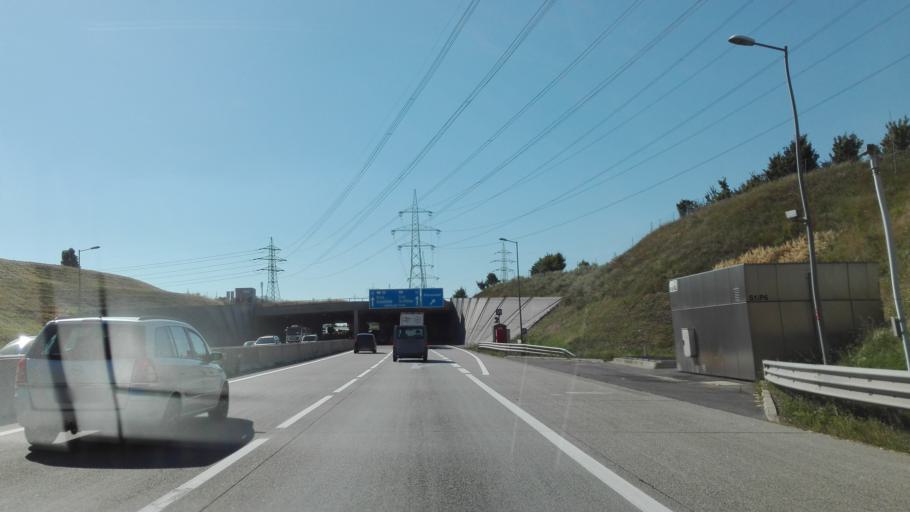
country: AT
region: Lower Austria
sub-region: Politischer Bezirk Wien-Umgebung
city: Leopoldsdorf
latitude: 48.1265
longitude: 16.3932
